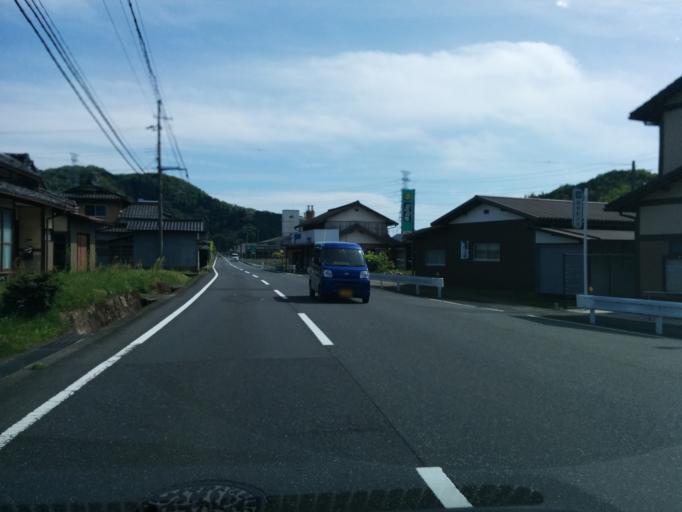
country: JP
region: Kyoto
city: Ayabe
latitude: 35.3530
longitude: 135.2209
